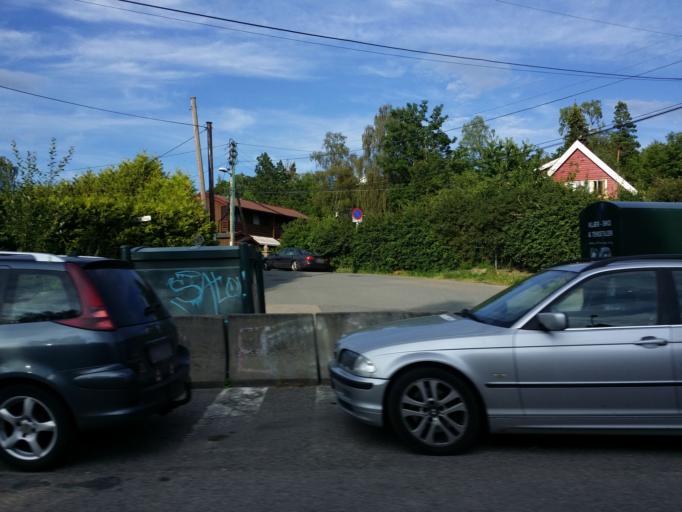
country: NO
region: Oslo
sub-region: Oslo
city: Oslo
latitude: 59.9079
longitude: 10.8509
